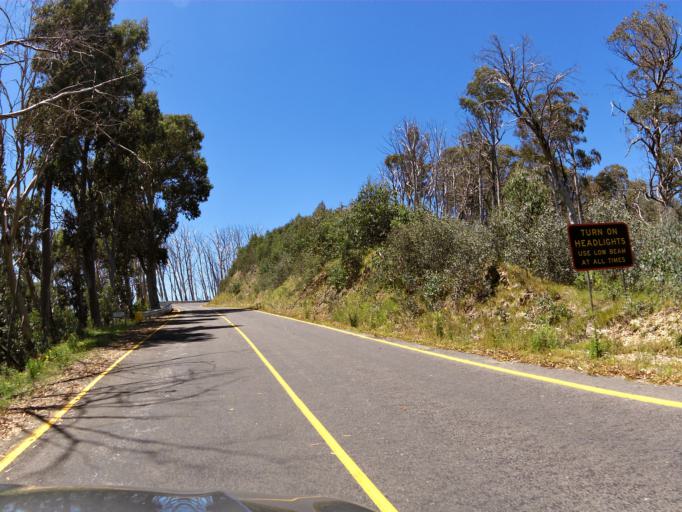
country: AU
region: Victoria
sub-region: Alpine
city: Mount Beauty
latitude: -37.0011
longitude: 147.0693
